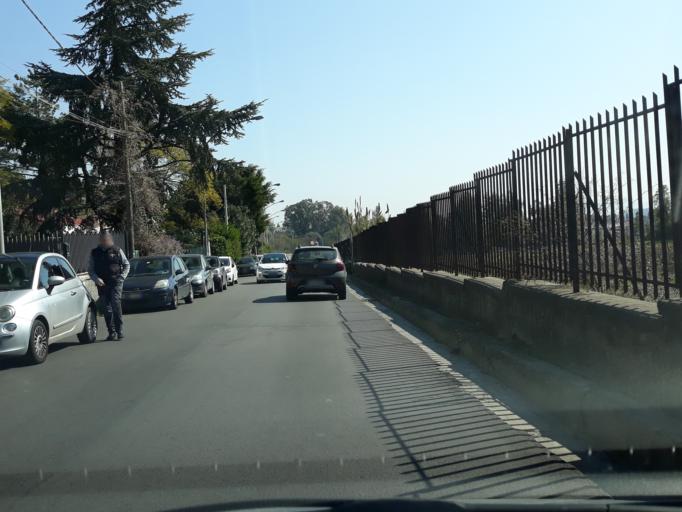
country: IT
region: Sicily
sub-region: Palermo
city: Piano dei Geli
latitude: 38.1186
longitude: 13.2984
